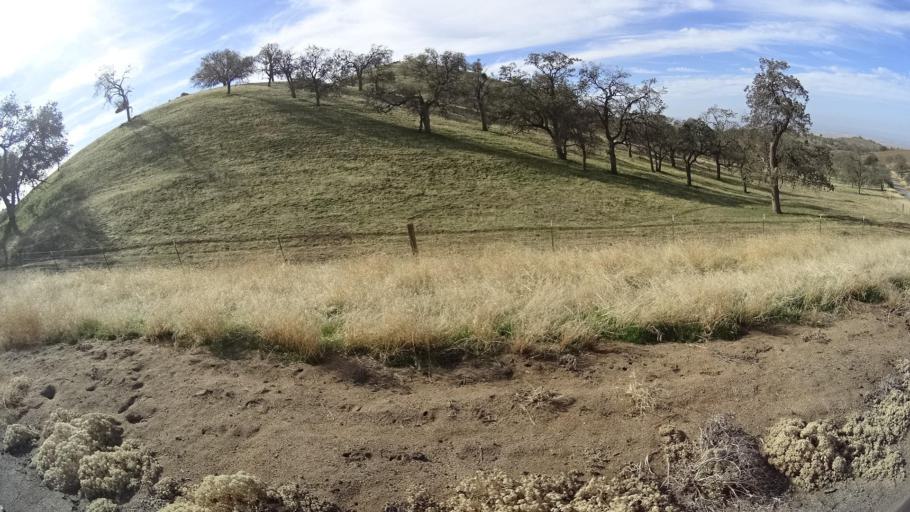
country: US
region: California
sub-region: Kern County
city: Oildale
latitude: 35.6094
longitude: -118.8312
